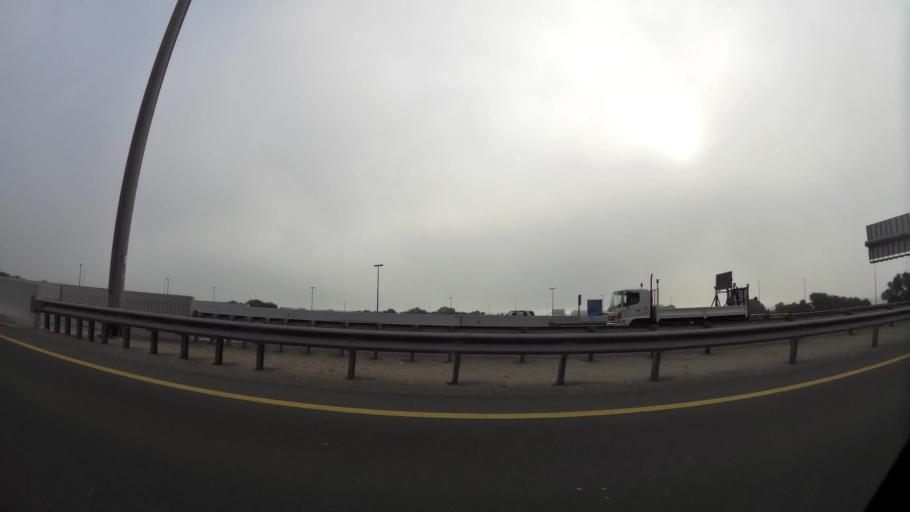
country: AE
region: Dubai
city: Dubai
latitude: 25.1800
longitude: 55.3159
